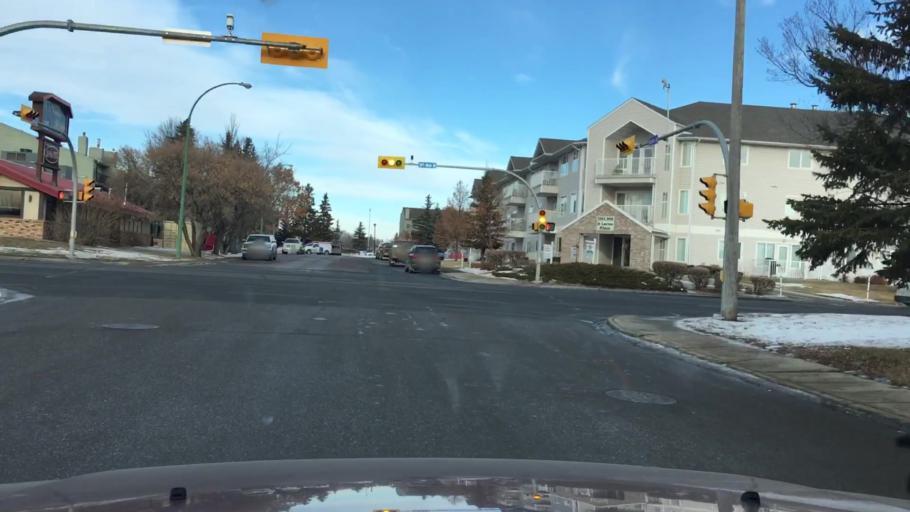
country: CA
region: Saskatchewan
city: Regina
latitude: 50.4841
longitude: -104.6137
